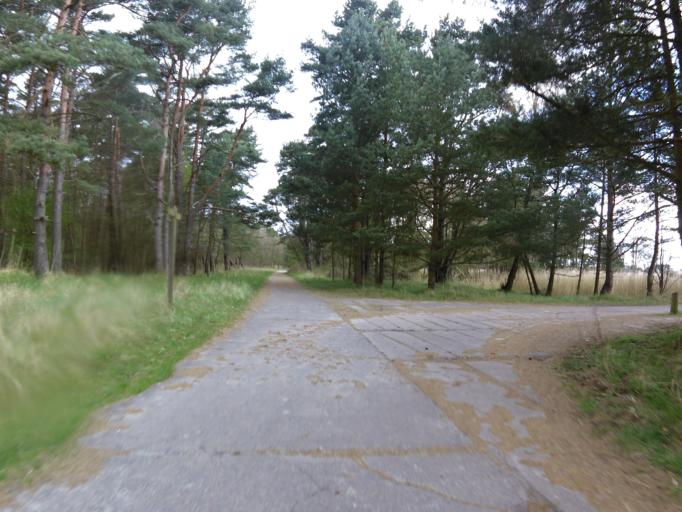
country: DE
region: Mecklenburg-Vorpommern
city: Ostseebad Prerow
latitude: 54.4675
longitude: 12.5221
